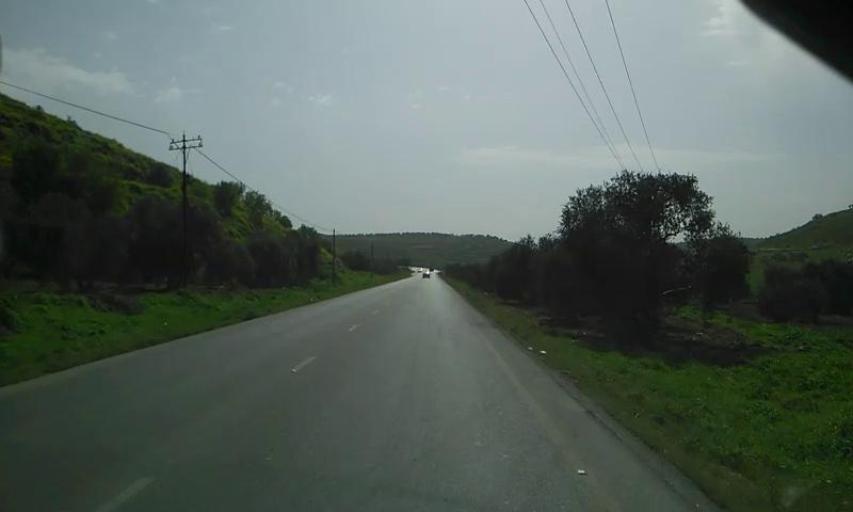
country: PS
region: West Bank
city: Mirkah
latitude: 32.3899
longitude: 35.2173
